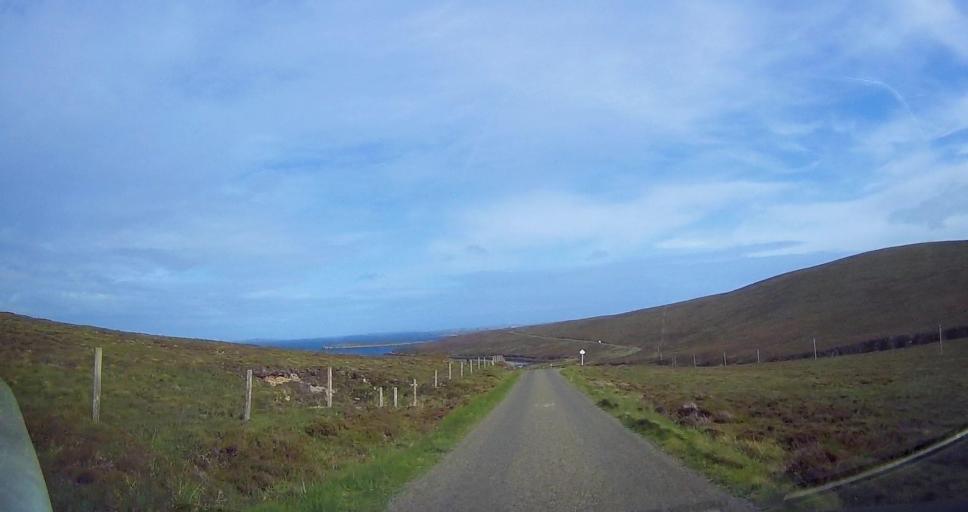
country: GB
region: Scotland
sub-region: Orkney Islands
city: Stromness
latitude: 58.8734
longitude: -3.2409
